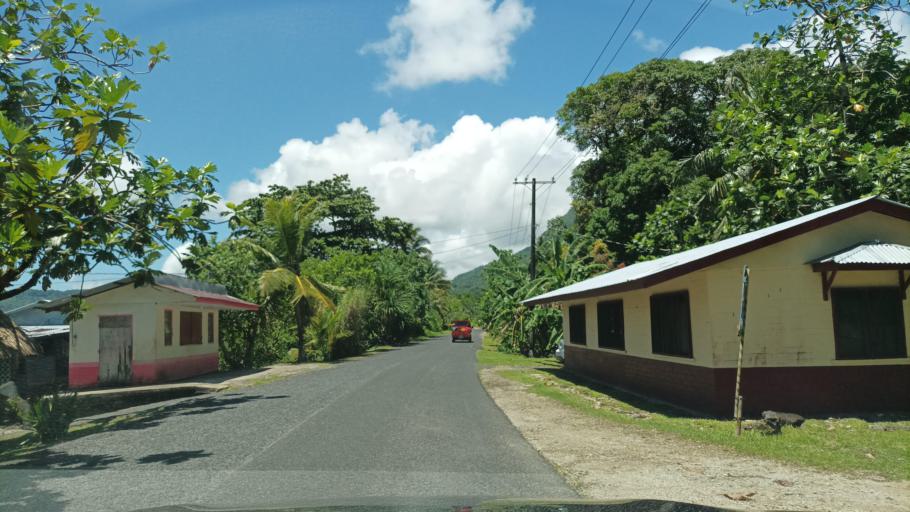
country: FM
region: Pohnpei
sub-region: Kolonia Municipality
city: Kolonia
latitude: 6.9533
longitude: 158.2775
